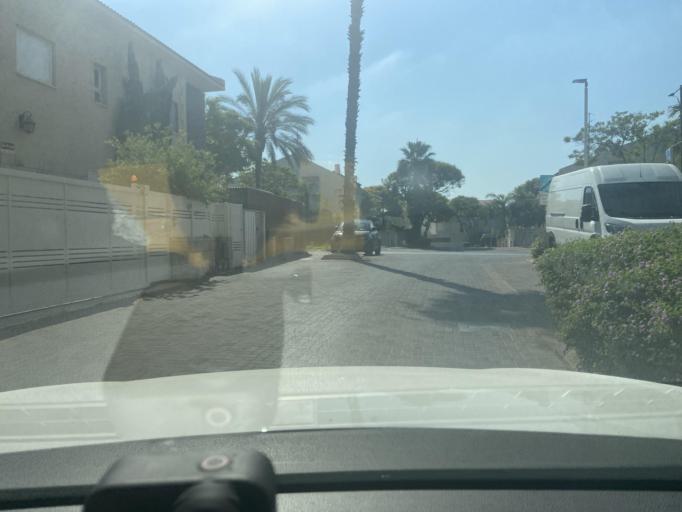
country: IL
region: Central District
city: Yehud
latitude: 32.0367
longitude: 34.8819
